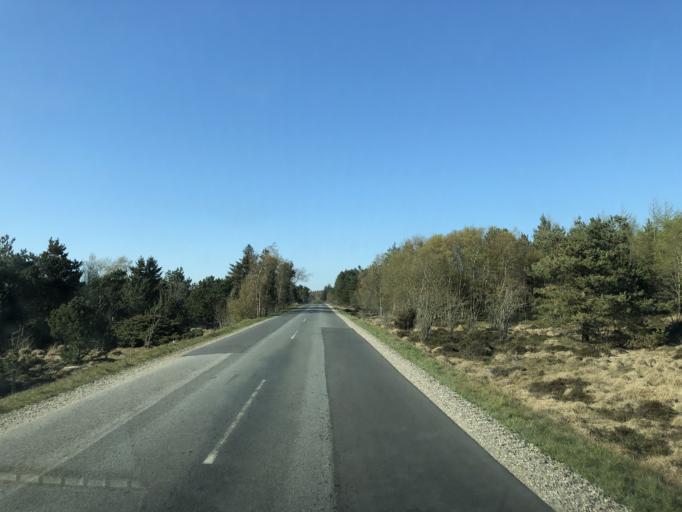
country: DK
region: Central Jutland
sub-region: Holstebro Kommune
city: Ulfborg
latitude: 56.2382
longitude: 8.3834
